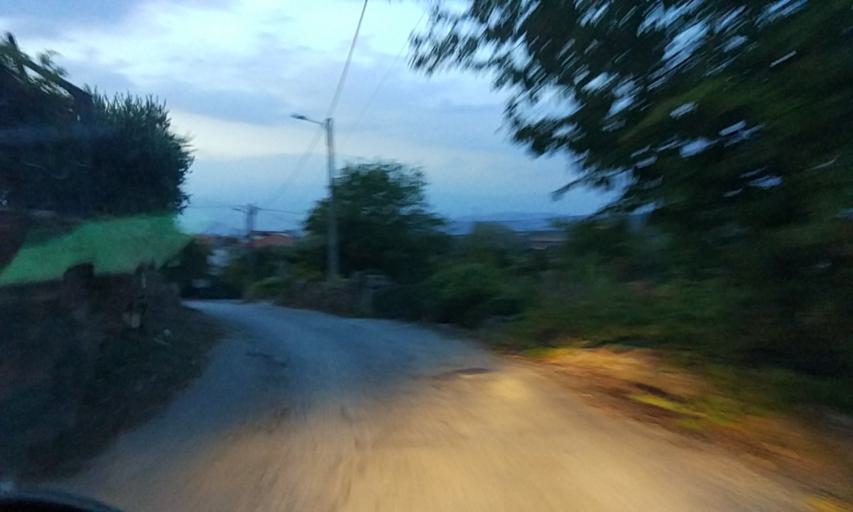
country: PT
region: Viseu
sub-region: Armamar
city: Armamar
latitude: 41.1156
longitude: -7.7146
